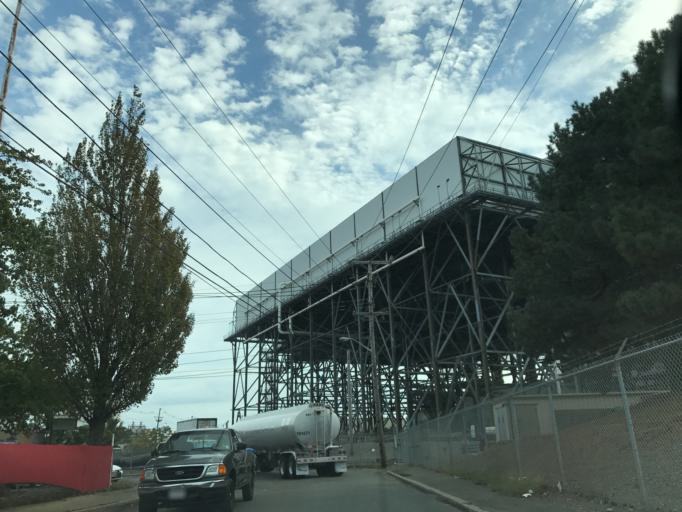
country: US
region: Massachusetts
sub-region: Middlesex County
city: Everett
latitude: 42.3933
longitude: -71.0657
